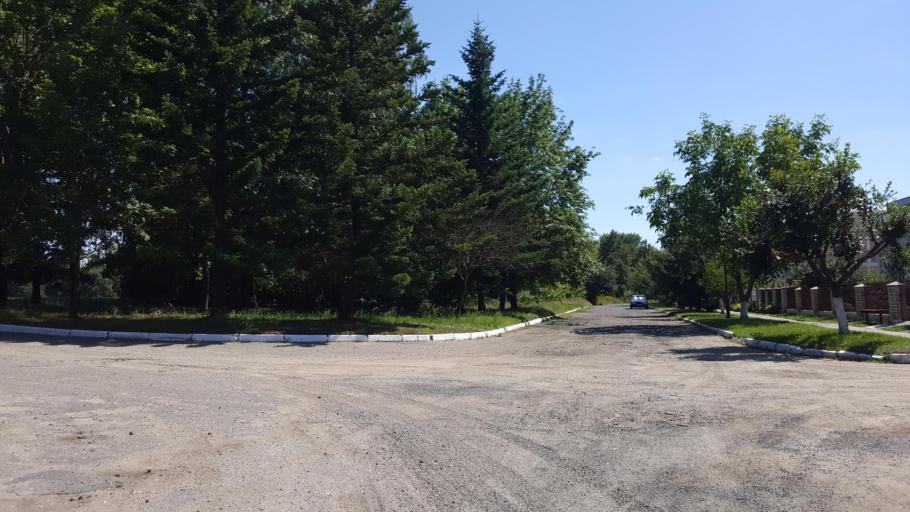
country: BY
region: Brest
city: Charnawchytsy
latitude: 52.2657
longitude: 23.5959
